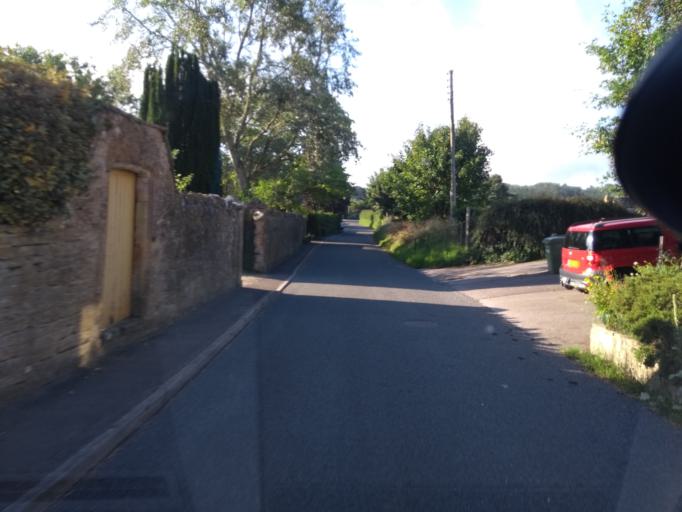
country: GB
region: England
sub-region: Somerset
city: South Petherton
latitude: 50.9659
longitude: -2.8094
